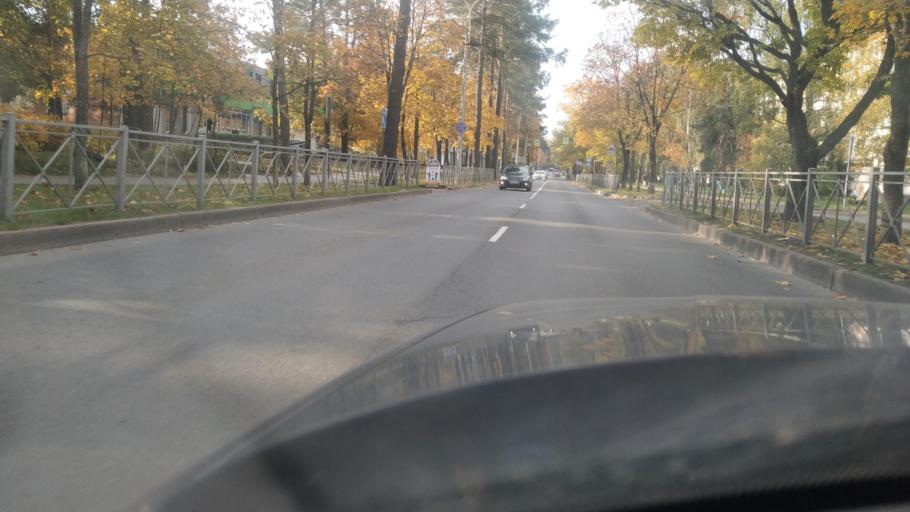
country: RU
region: Leningrad
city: Sosnovyy Bor
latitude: 59.8911
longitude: 29.0927
